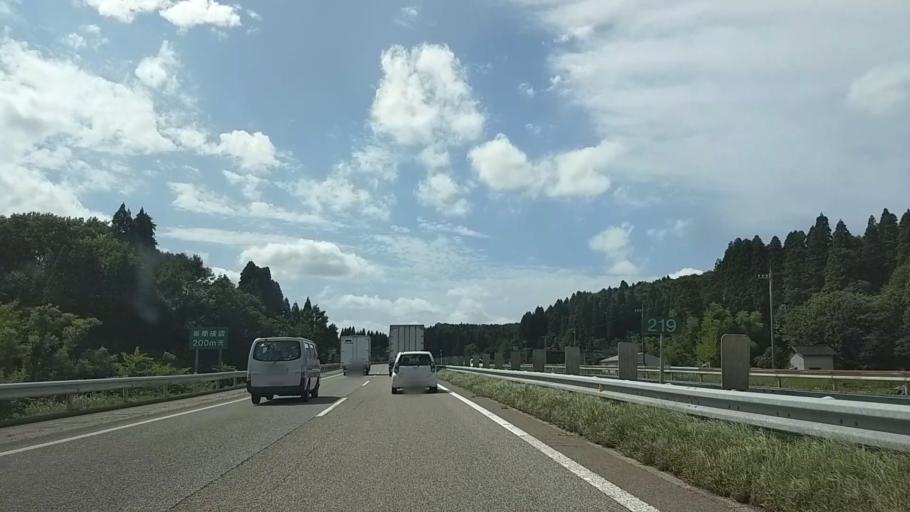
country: JP
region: Toyama
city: Takaoka
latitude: 36.6850
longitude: 137.0558
